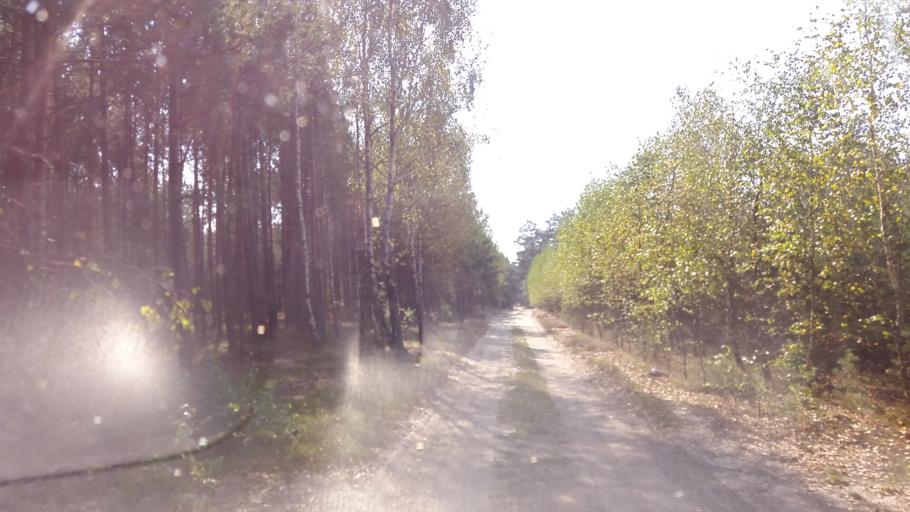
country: PL
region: West Pomeranian Voivodeship
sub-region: Powiat drawski
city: Kalisz Pomorski
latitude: 53.2197
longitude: 15.9027
